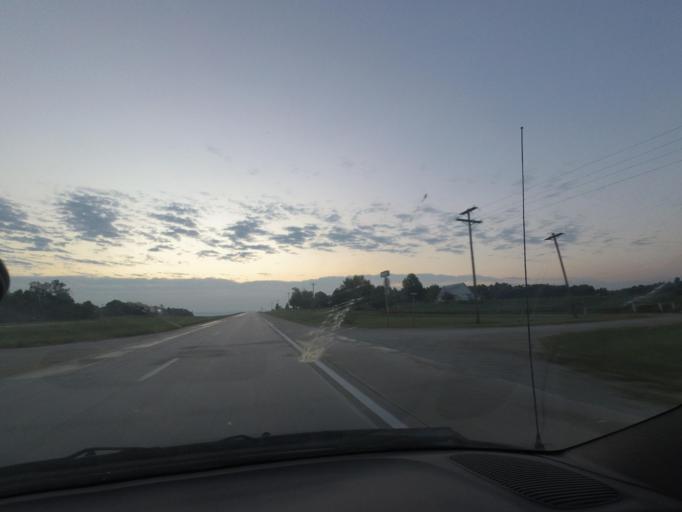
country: US
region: Missouri
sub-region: Macon County
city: Macon
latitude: 39.7595
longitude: -92.6695
